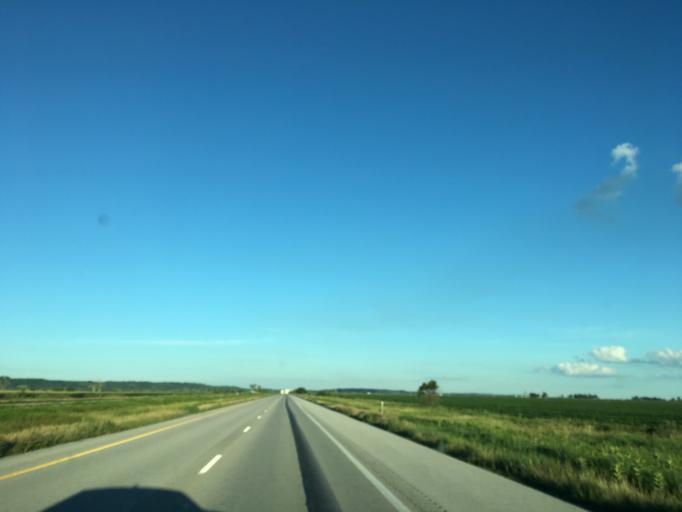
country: US
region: Iowa
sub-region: Fremont County
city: Hamburg
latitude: 40.6370
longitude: -95.7314
